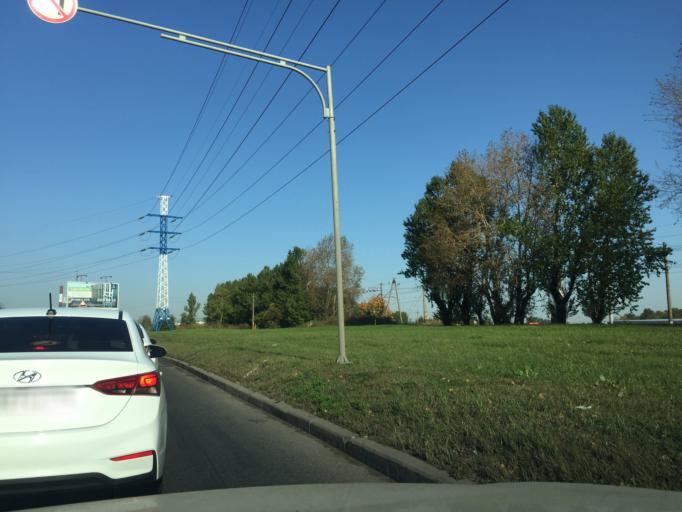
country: RU
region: St.-Petersburg
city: Centralniy
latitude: 59.8932
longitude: 30.3438
